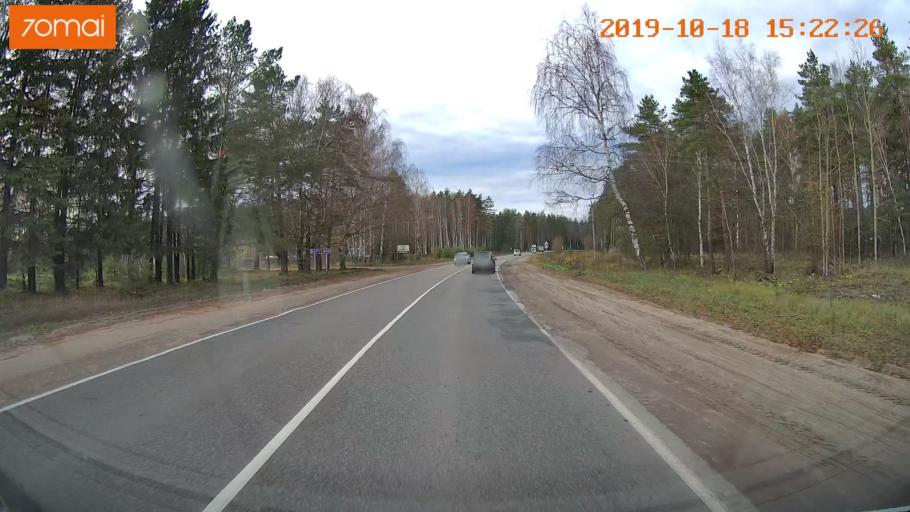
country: RU
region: Vladimir
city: Anopino
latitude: 55.7077
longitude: 40.7317
